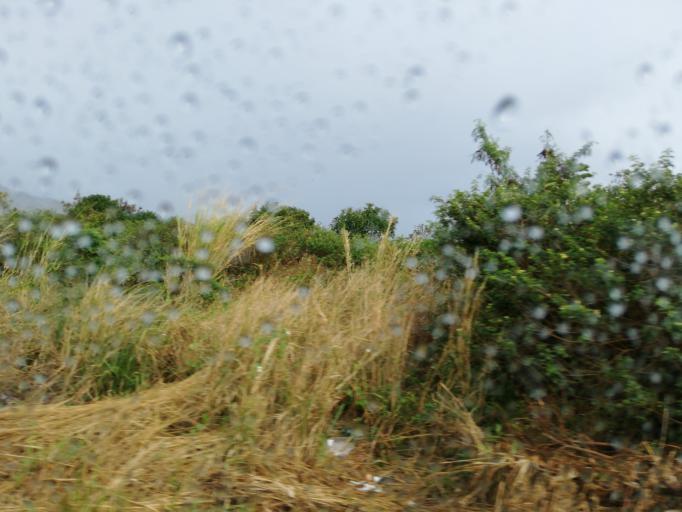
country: MU
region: Pamplemousses
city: Long Mountain
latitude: -20.1295
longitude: 57.5659
